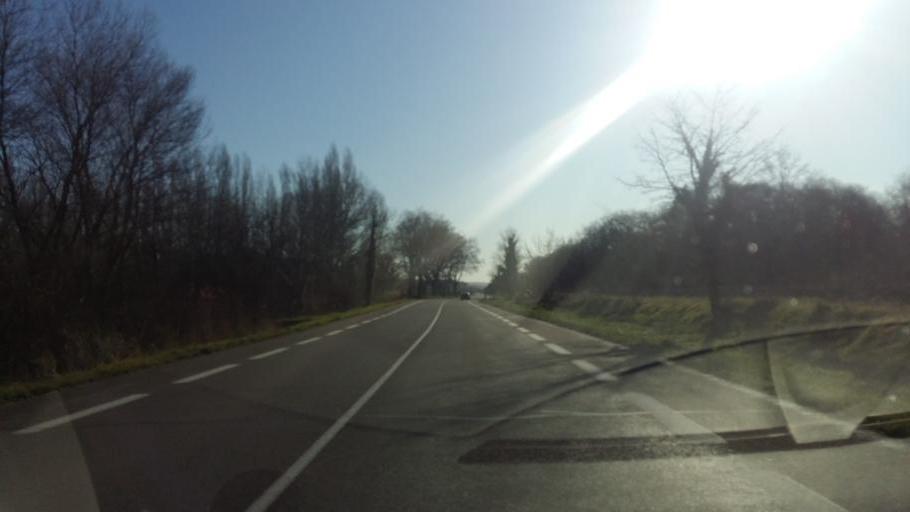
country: FR
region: Provence-Alpes-Cote d'Azur
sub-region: Departement du Vaucluse
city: Lauris
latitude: 43.7388
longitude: 5.3290
